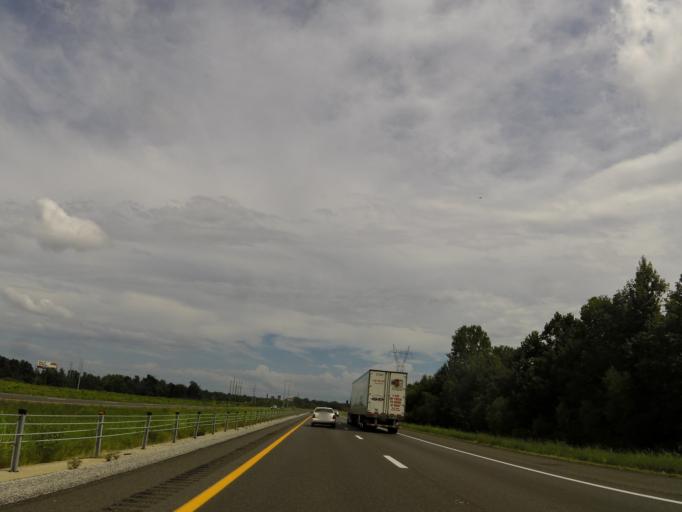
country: US
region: Kentucky
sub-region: McCracken County
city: Hendron
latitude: 37.0341
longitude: -88.6260
